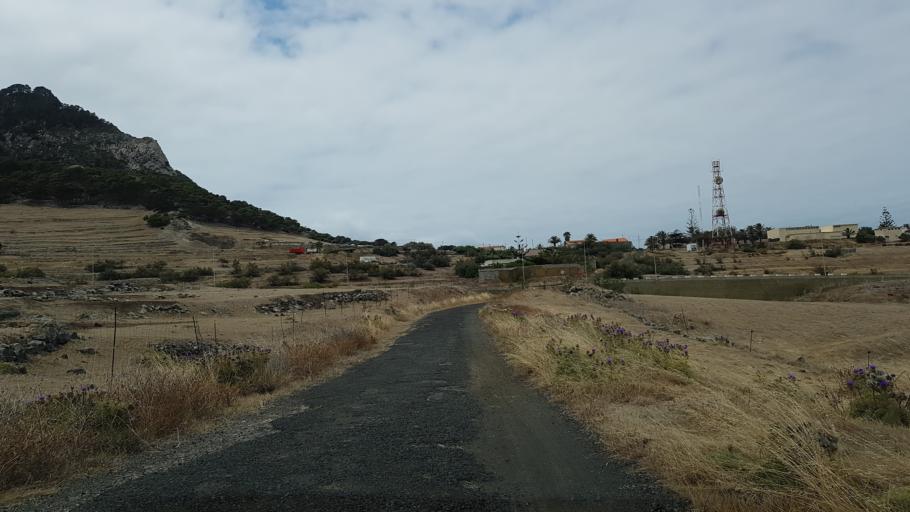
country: PT
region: Madeira
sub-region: Porto Santo
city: Camacha
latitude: 33.0899
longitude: -16.3364
